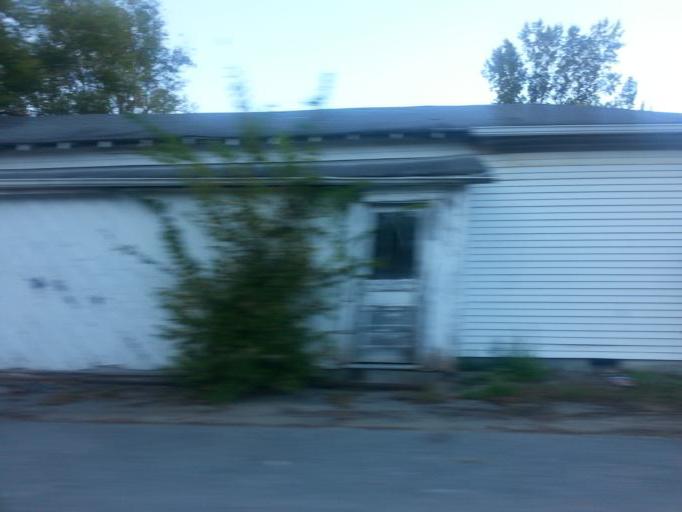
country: US
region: Tennessee
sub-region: Anderson County
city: Rocky Top
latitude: 36.2496
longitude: -84.1694
